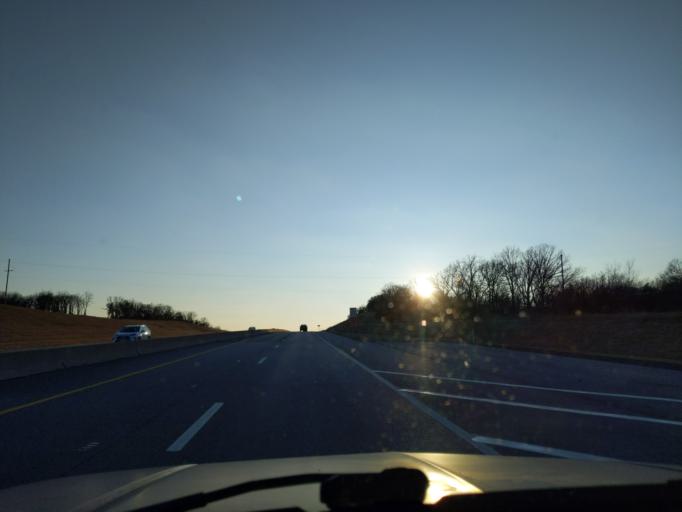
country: US
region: Oklahoma
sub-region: Creek County
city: Kellyville
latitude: 35.9065
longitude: -96.3055
